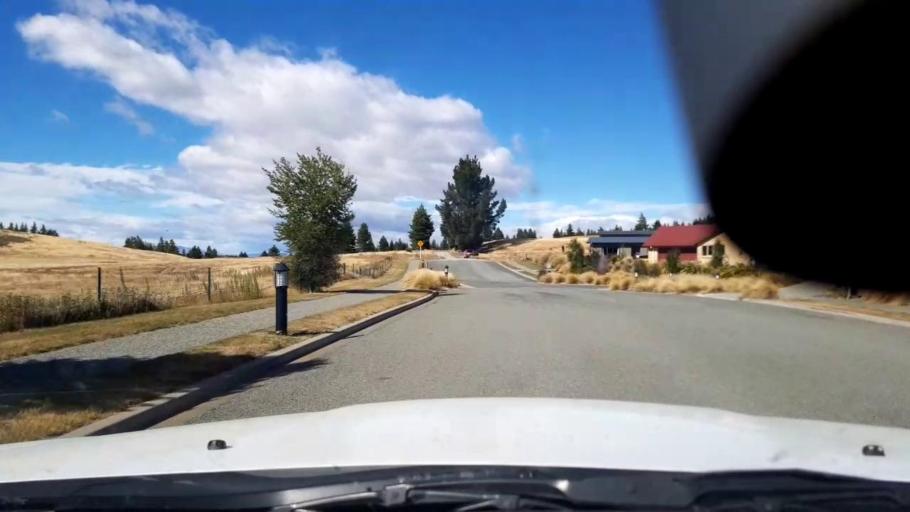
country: NZ
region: Canterbury
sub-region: Timaru District
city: Pleasant Point
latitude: -44.0079
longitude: 170.4741
